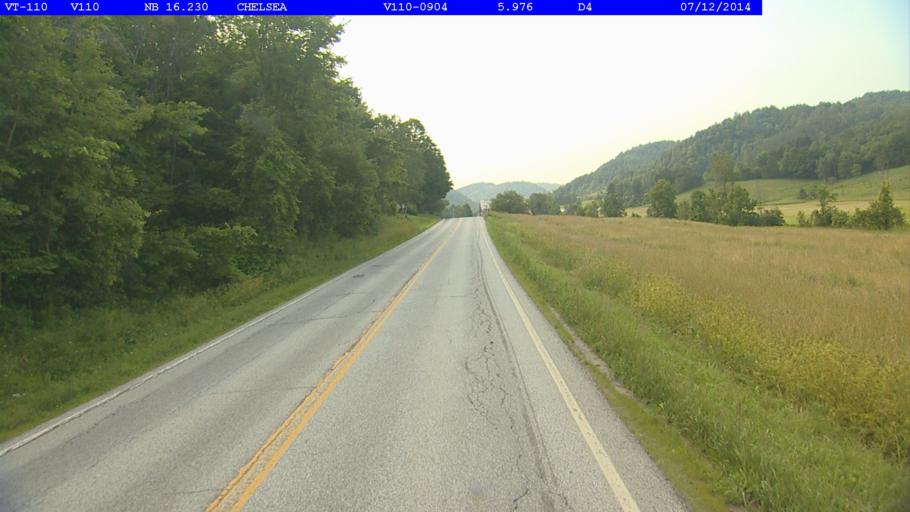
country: US
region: Vermont
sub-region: Orange County
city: Chelsea
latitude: 44.0269
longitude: -72.4719
